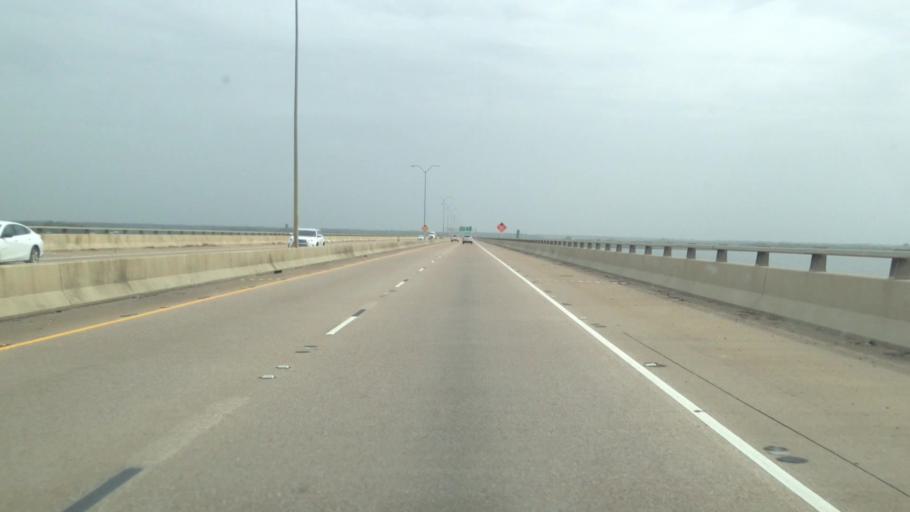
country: US
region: Louisiana
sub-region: Caddo Parish
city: Shreveport
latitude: 32.5011
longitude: -93.8183
